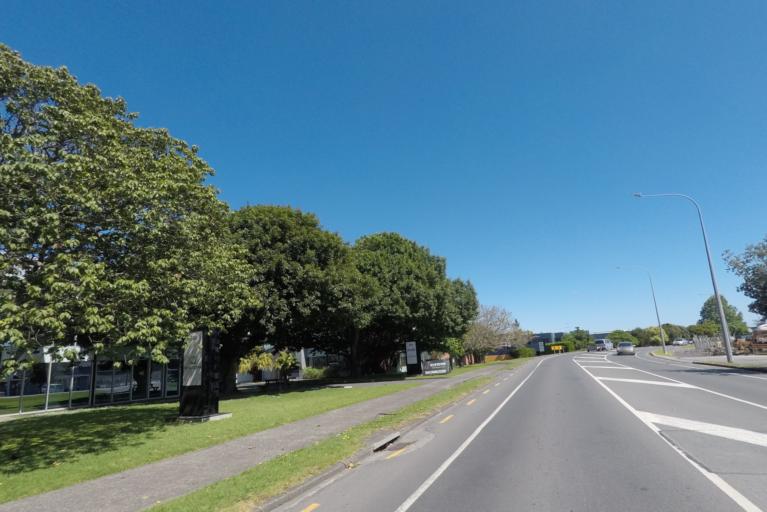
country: NZ
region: Auckland
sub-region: Auckland
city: Rosebank
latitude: -36.8782
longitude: 174.6704
